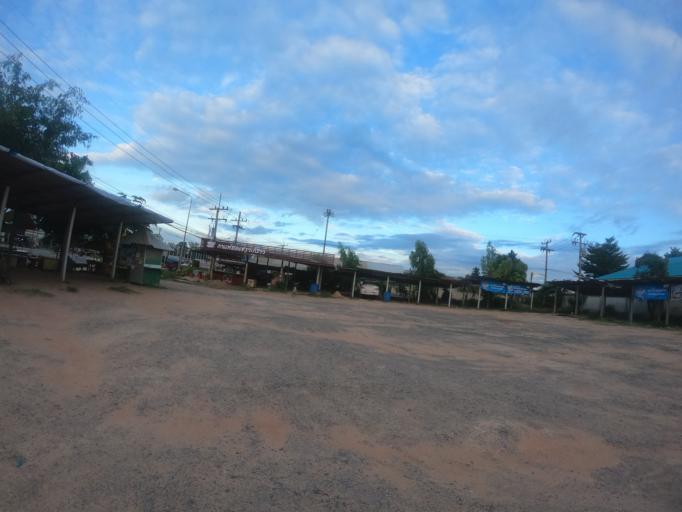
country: TH
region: Surin
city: Kap Choeng
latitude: 14.4535
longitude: 103.6878
